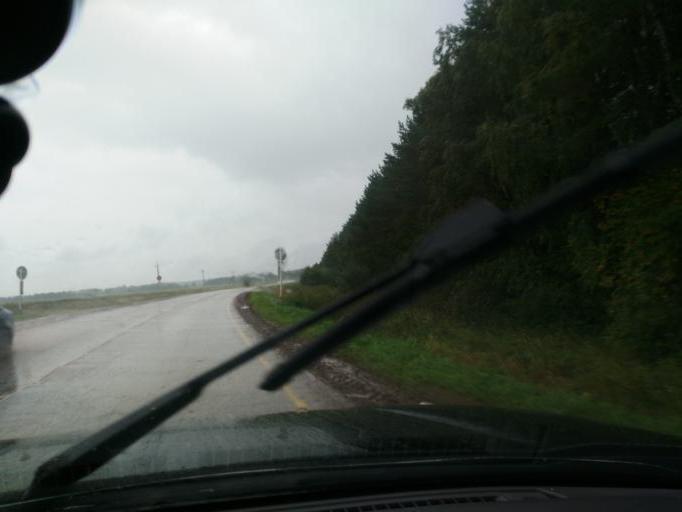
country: RU
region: Perm
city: Osa
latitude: 57.2906
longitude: 55.5828
